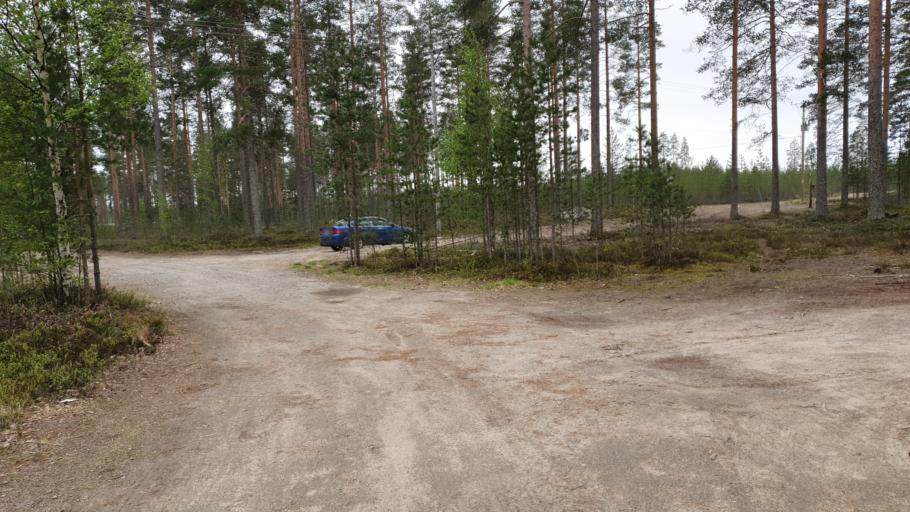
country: FI
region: Kainuu
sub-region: Kehys-Kainuu
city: Kuhmo
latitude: 64.0969
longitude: 29.4654
